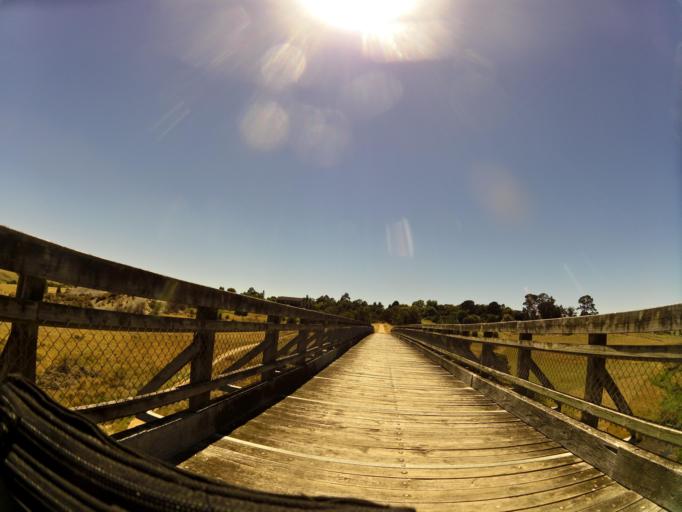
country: AU
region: Victoria
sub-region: Ballarat North
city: Delacombe
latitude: -37.7033
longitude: 143.6382
